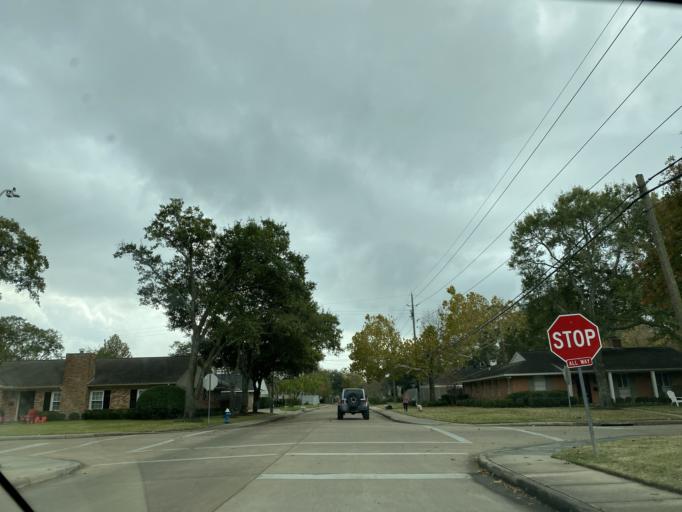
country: US
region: Texas
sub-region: Harris County
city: Hunters Creek Village
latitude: 29.7436
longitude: -95.4925
